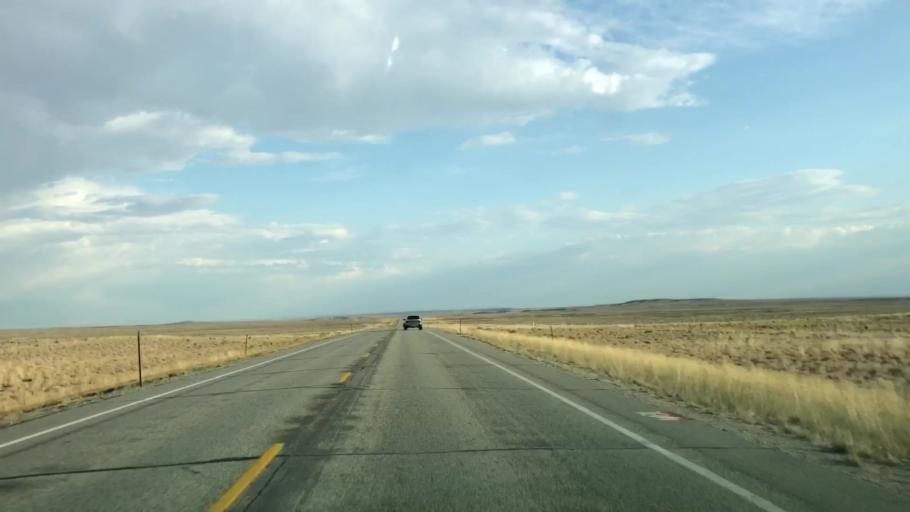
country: US
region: Wyoming
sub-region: Sublette County
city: Pinedale
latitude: 42.3881
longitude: -109.5389
